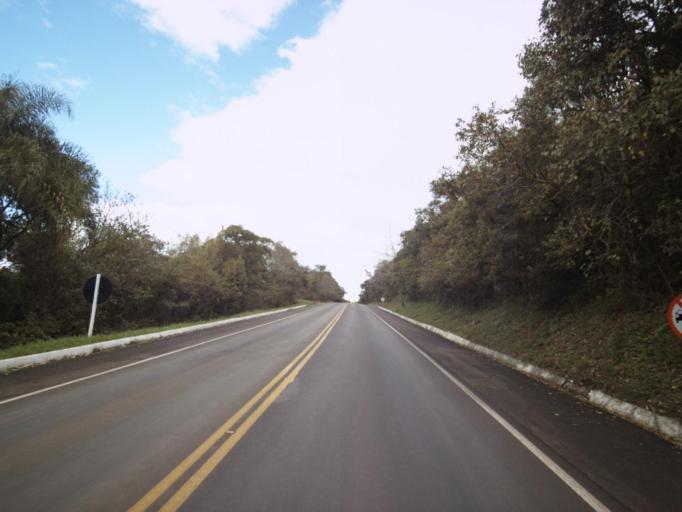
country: BR
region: Santa Catarina
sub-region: Concordia
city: Concordia
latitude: -27.3553
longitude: -51.9883
